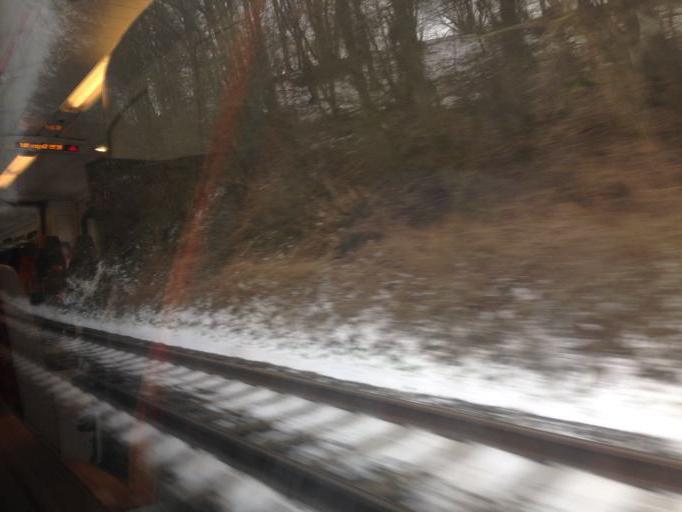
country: DE
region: Hesse
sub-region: Regierungsbezirk Giessen
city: Ehringshausen
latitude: 50.6115
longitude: 8.3628
